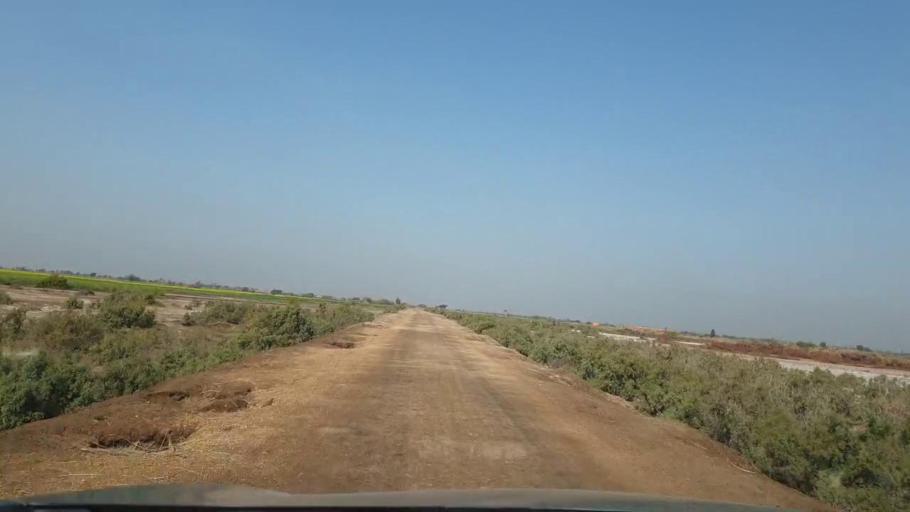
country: PK
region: Sindh
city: Berani
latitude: 25.7043
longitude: 68.8663
